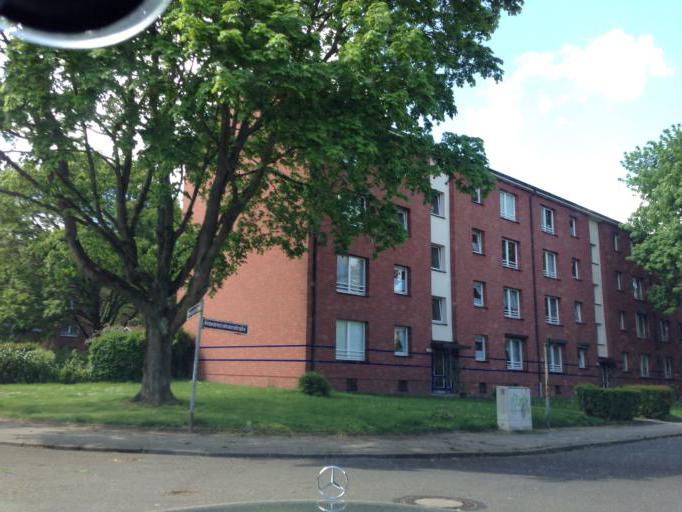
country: DE
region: Schleswig-Holstein
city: Barsbuettel
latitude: 53.5882
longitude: 10.1532
